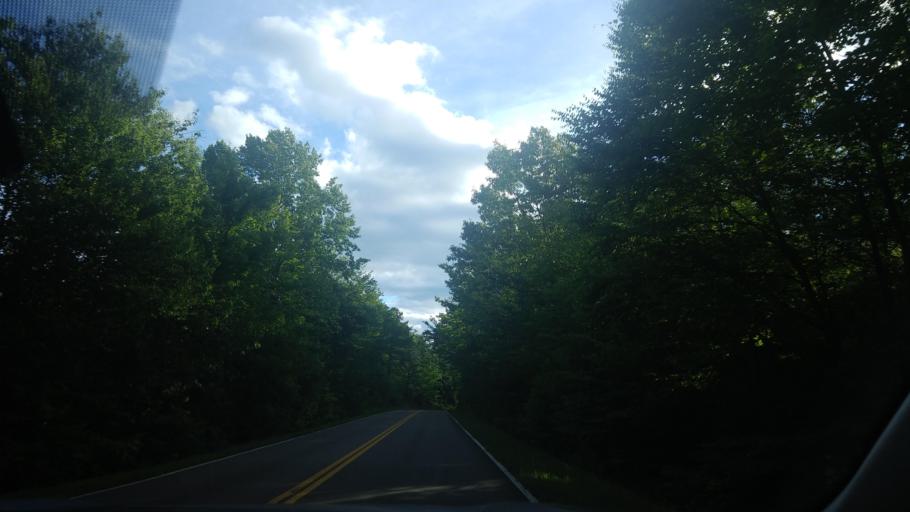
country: US
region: Tennessee
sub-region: Cocke County
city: Newport
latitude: 35.8170
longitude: -83.2186
